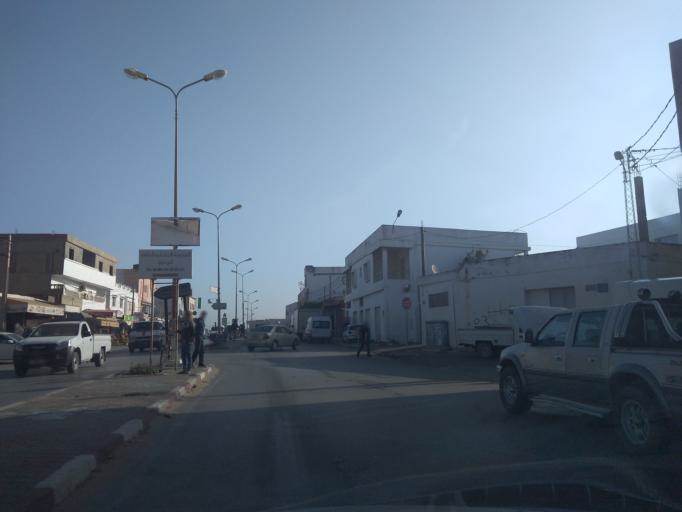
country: TN
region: Manouba
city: Manouba
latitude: 36.7894
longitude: 10.0883
